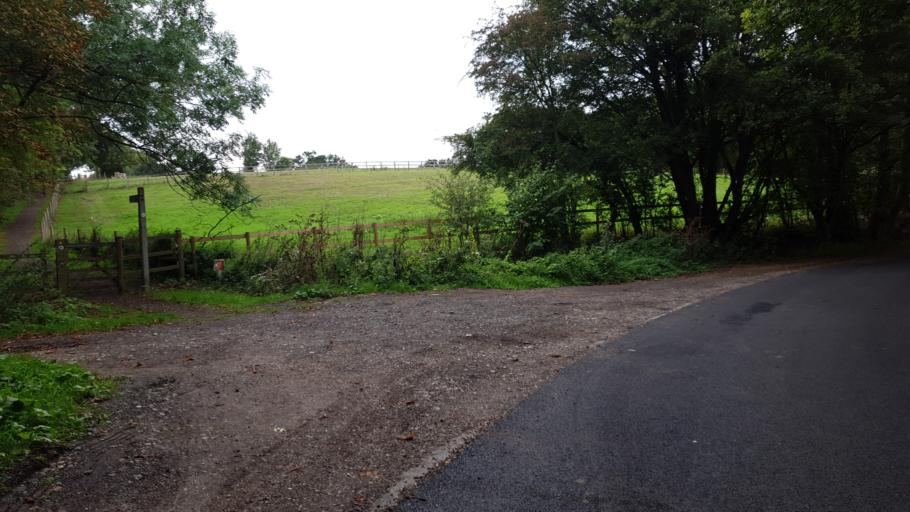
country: GB
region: England
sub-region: Suffolk
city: East Bergholt
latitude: 51.9467
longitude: 1.0063
